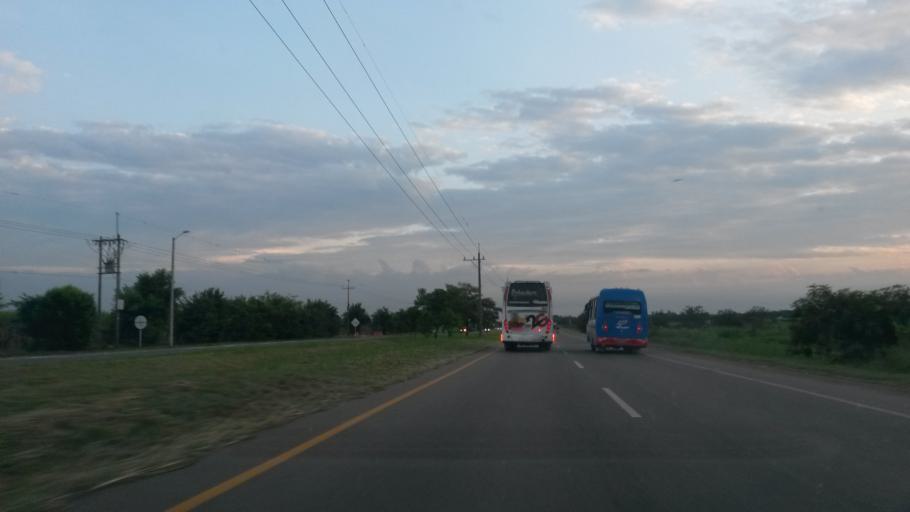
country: CO
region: Cauca
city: Puerto Tejada
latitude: 3.1358
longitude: -76.4628
